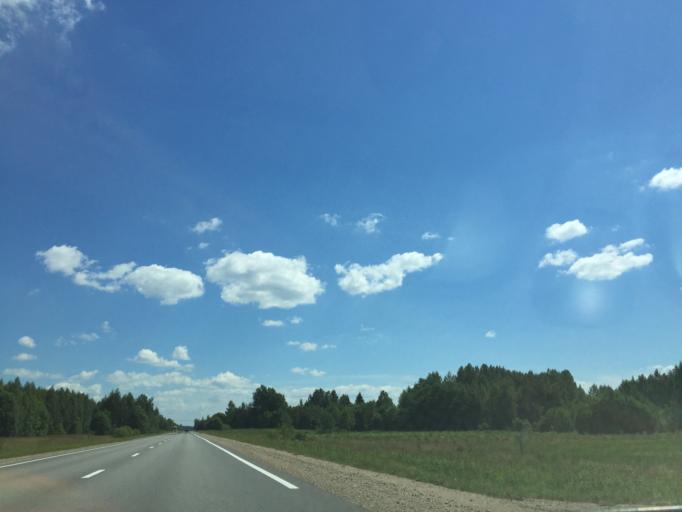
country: LV
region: Rezekne
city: Rezekne
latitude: 56.4887
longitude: 27.2753
